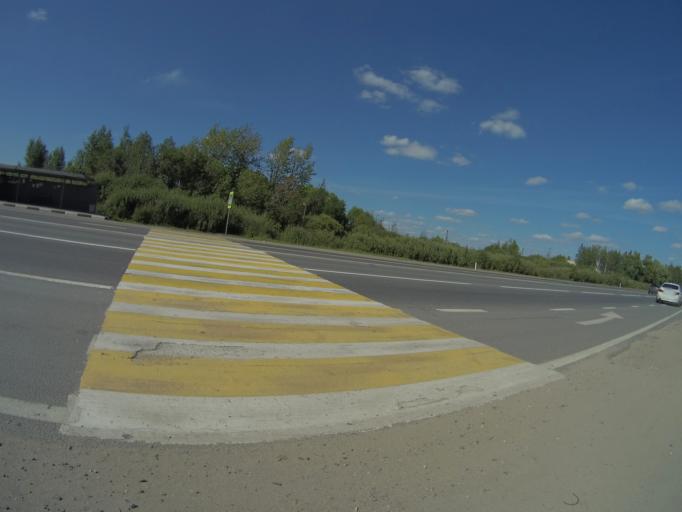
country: RU
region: Vladimir
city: Vorsha
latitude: 56.0854
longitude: 40.2159
